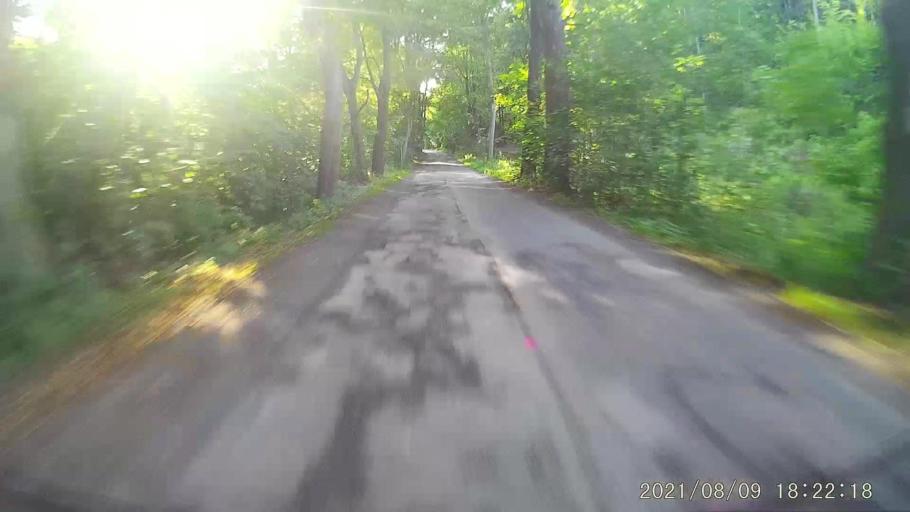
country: PL
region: Lower Silesian Voivodeship
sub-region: Powiat zabkowicki
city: Bardo
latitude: 50.5053
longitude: 16.7094
